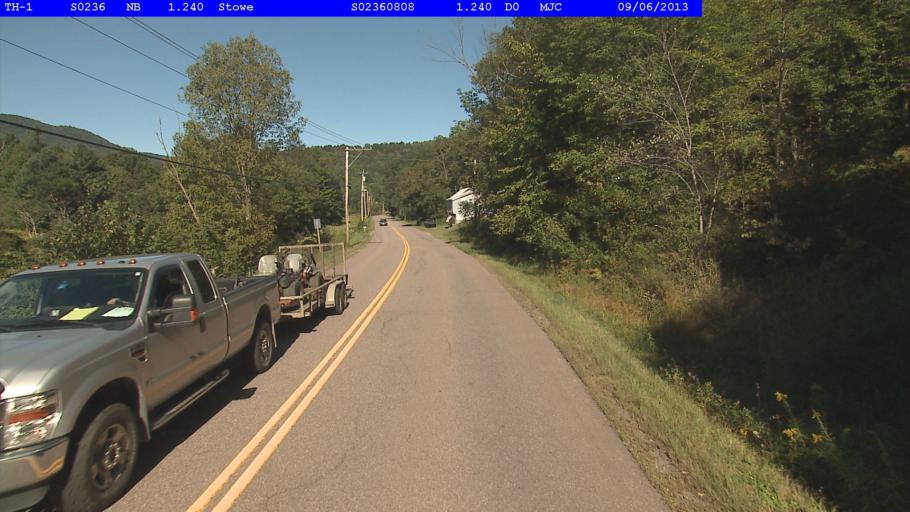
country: US
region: Vermont
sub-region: Washington County
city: Waterbury
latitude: 44.4456
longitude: -72.7291
